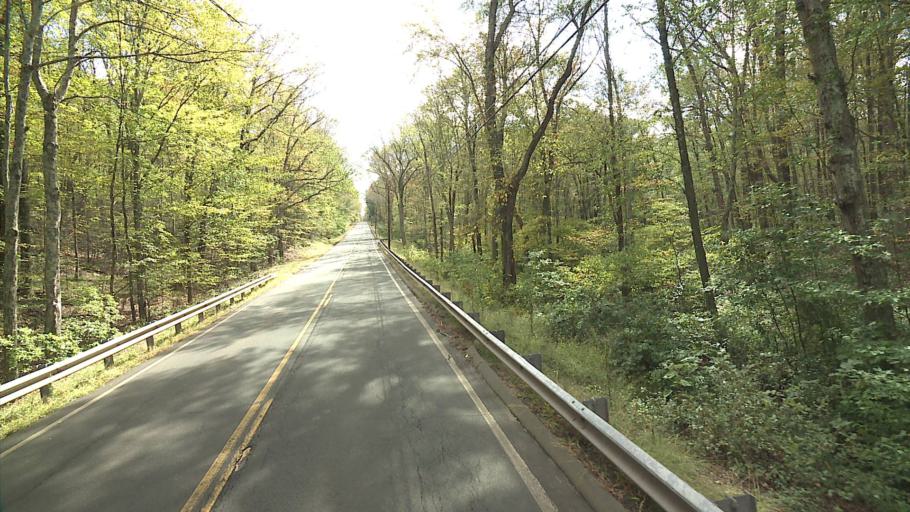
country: US
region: Connecticut
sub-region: Middlesex County
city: Durham
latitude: 41.4300
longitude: -72.6385
